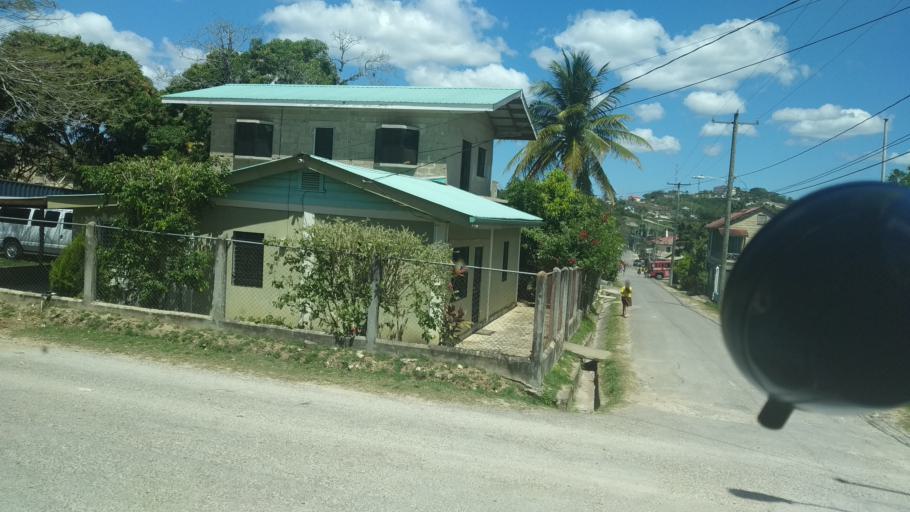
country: BZ
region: Cayo
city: Benque Viejo del Carmen
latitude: 17.0727
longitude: -89.1407
